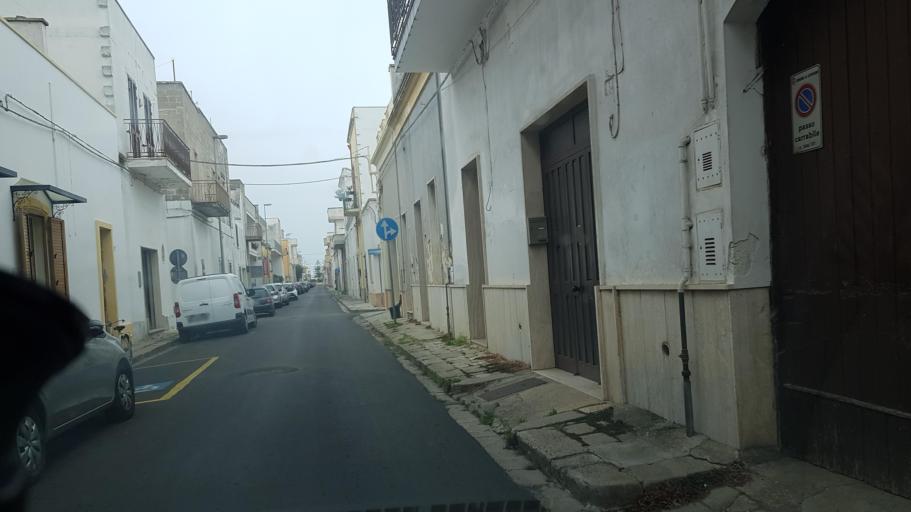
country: IT
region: Apulia
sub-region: Provincia di Lecce
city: Leverano
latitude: 40.2900
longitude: 18.0021
